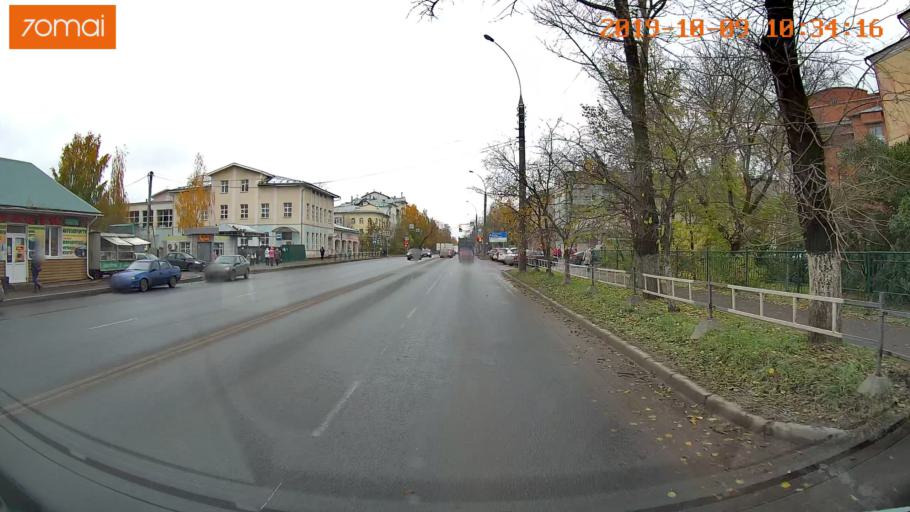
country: RU
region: Vologda
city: Vologda
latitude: 59.2254
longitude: 39.8689
